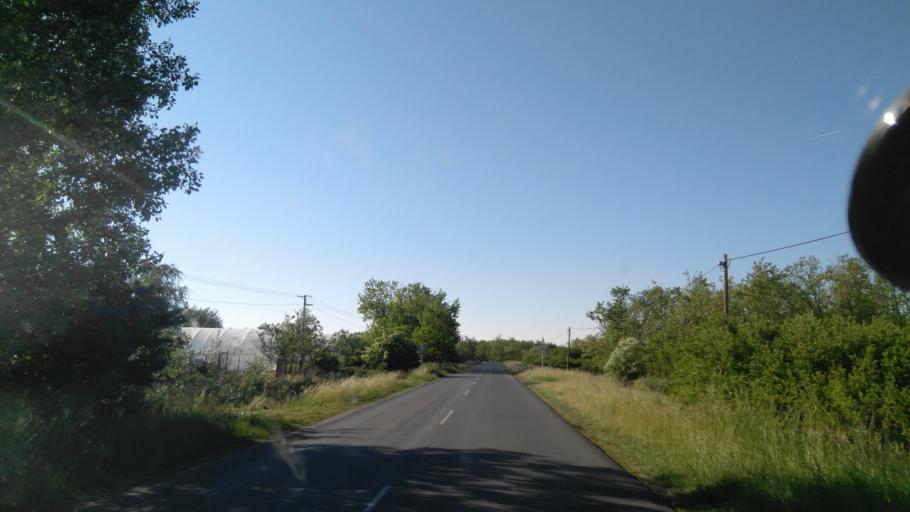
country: HU
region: Bekes
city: Gyula
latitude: 46.6087
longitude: 21.2721
